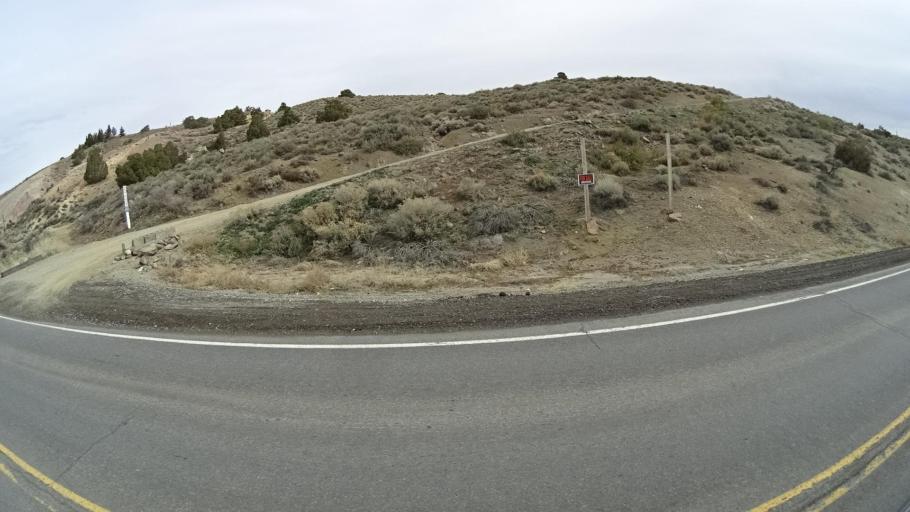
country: US
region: Nevada
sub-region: Washoe County
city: Sun Valley
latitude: 39.6002
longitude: -119.7937
